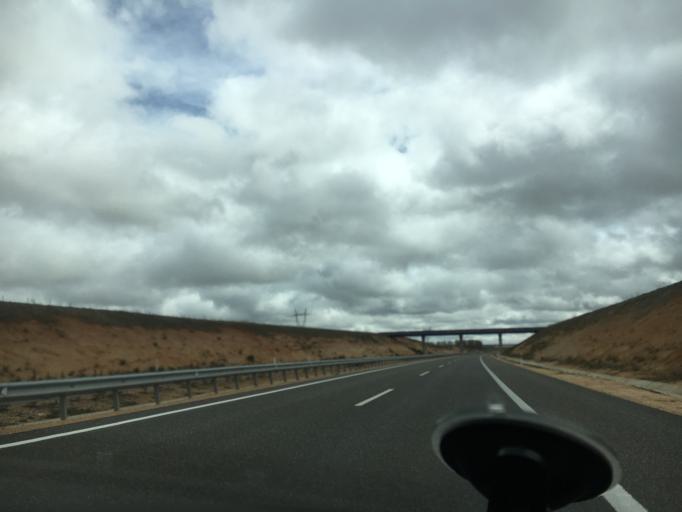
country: ES
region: Castille and Leon
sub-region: Provincia de Zamora
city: Montamarta
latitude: 41.6609
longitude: -5.7977
